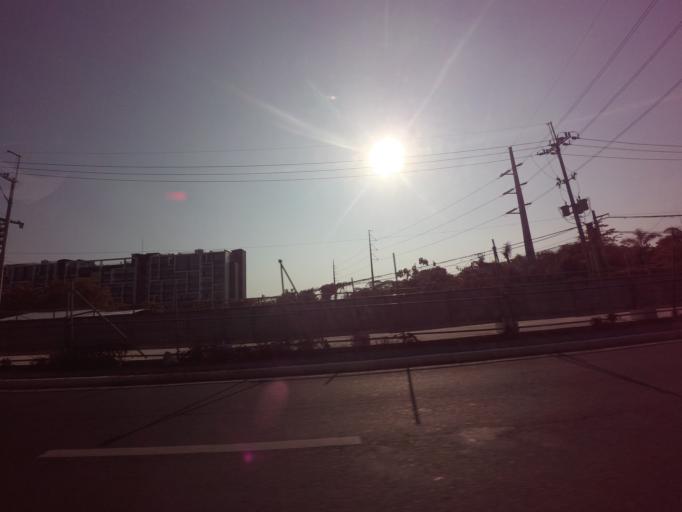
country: PH
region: Metro Manila
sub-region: Makati City
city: Makati City
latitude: 14.5404
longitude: 121.0471
